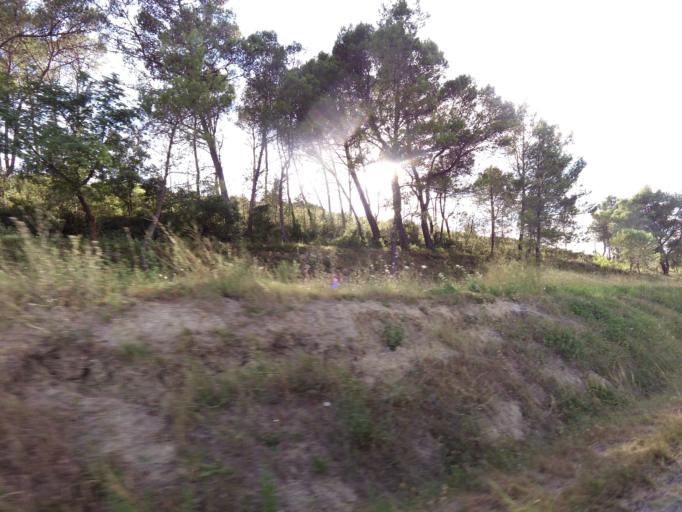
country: FR
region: Languedoc-Roussillon
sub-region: Departement du Gard
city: Congenies
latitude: 43.7939
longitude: 4.1634
